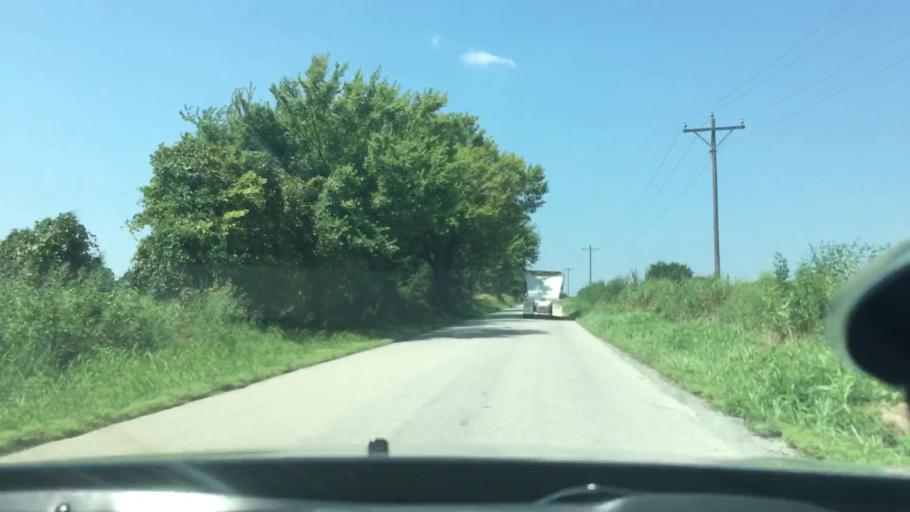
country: US
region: Oklahoma
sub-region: Bryan County
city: Durant
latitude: 34.2588
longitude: -96.4006
